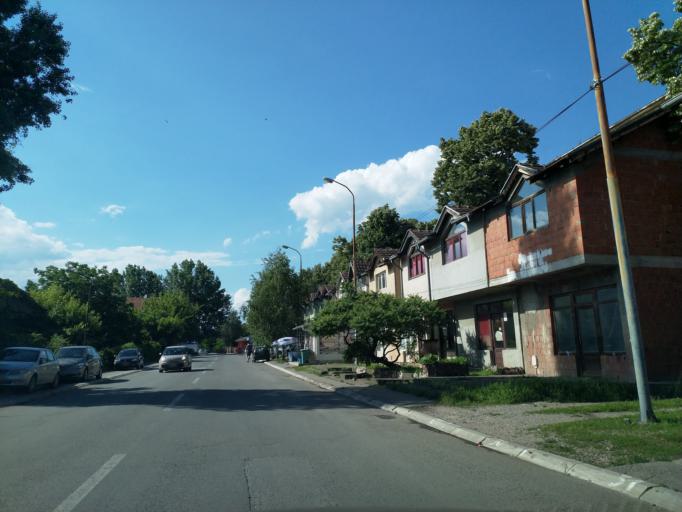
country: RS
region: Central Serbia
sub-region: Pomoravski Okrug
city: Paracin
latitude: 43.8570
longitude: 21.4064
